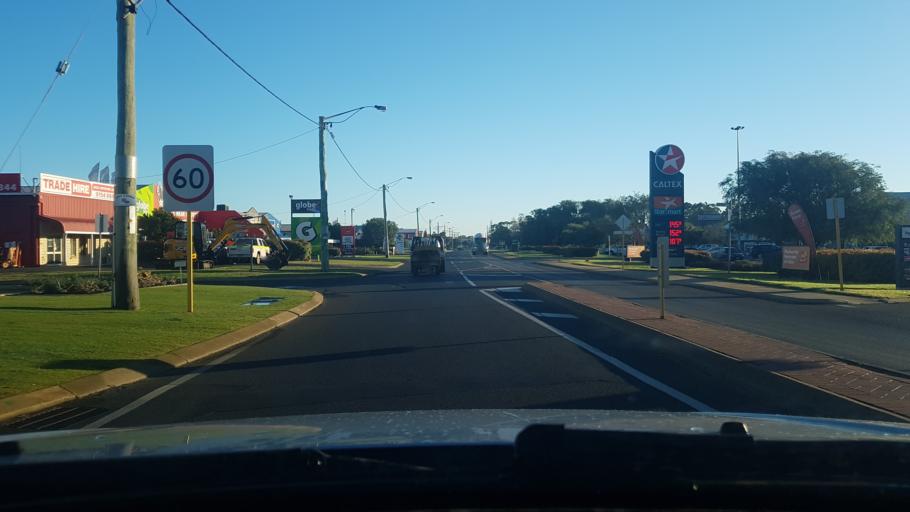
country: AU
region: Western Australia
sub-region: Busselton
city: Busselton
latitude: -33.6681
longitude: 115.3495
